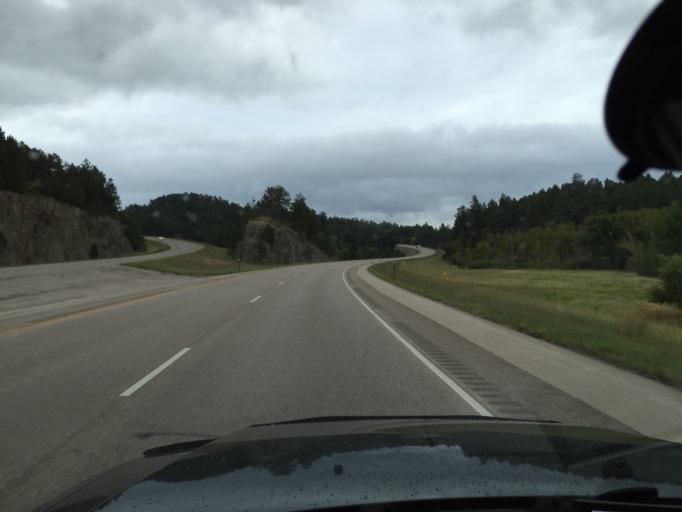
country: US
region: South Dakota
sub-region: Pennington County
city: Colonial Pine Hills
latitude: 43.9428
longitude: -103.3900
